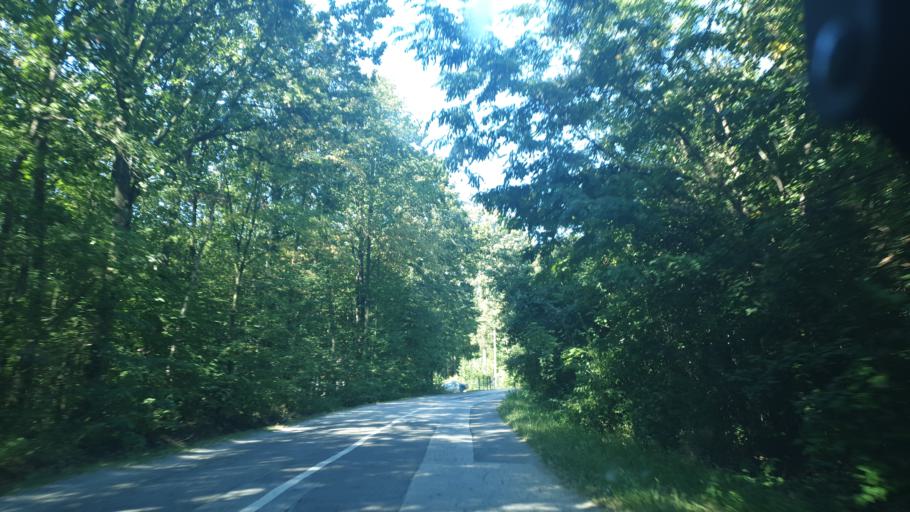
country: RS
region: Central Serbia
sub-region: Kolubarski Okrug
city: Lajkovac
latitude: 44.3088
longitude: 20.1693
